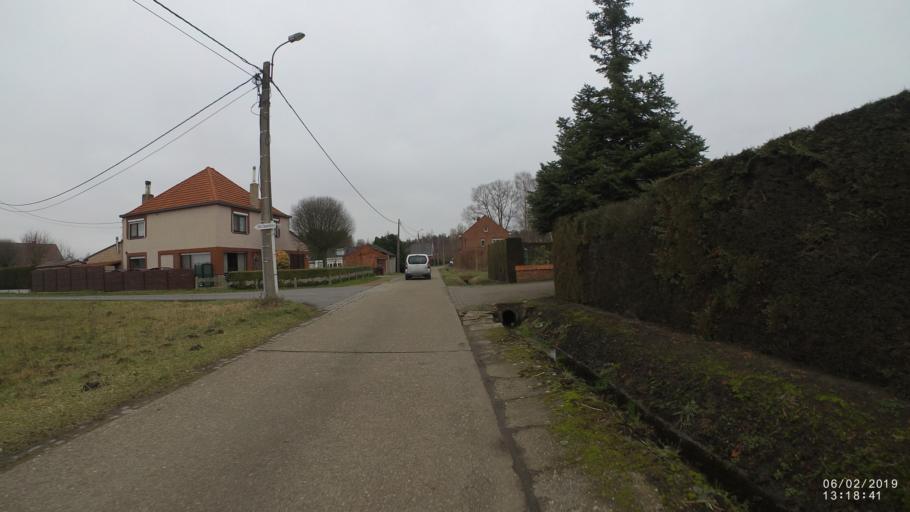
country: BE
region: Flanders
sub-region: Provincie Vlaams-Brabant
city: Begijnendijk
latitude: 51.0211
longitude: 4.8154
